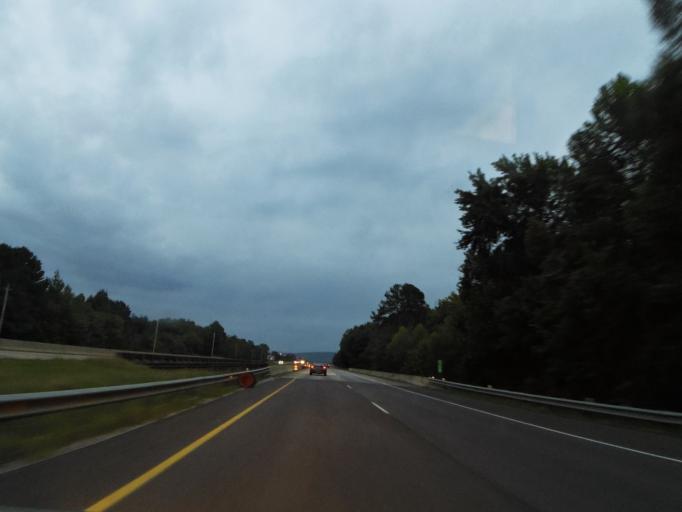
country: US
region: Alabama
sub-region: Madison County
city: Moores Mill
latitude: 34.7435
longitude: -86.4463
